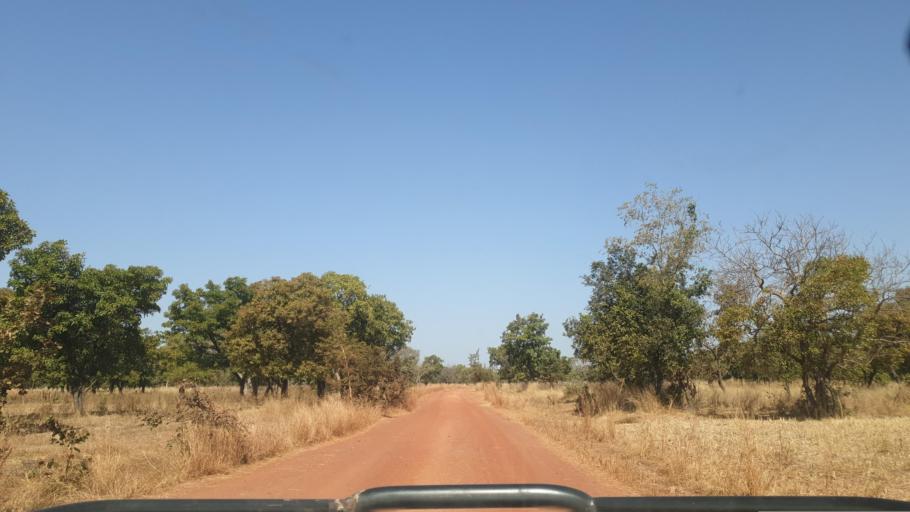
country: ML
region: Koulikoro
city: Dioila
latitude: 11.8992
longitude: -6.9812
